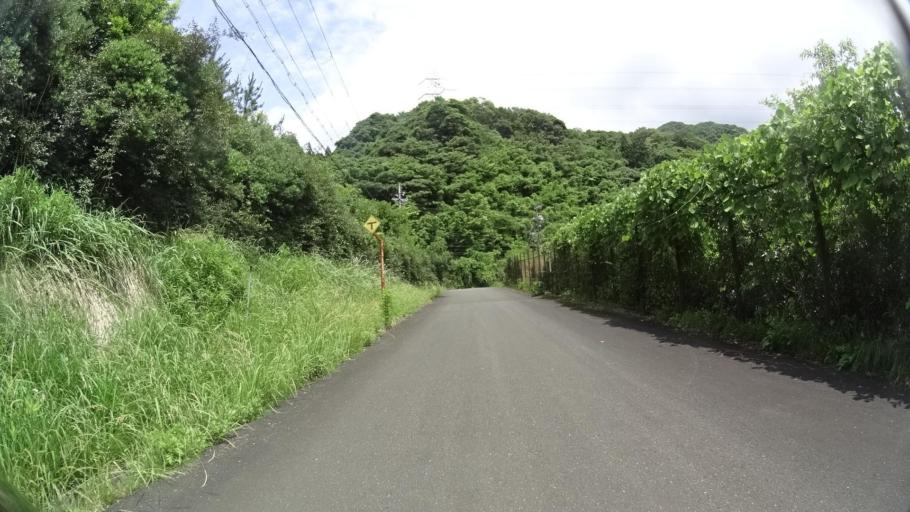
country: JP
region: Kyoto
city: Maizuru
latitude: 35.5328
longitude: 135.3462
